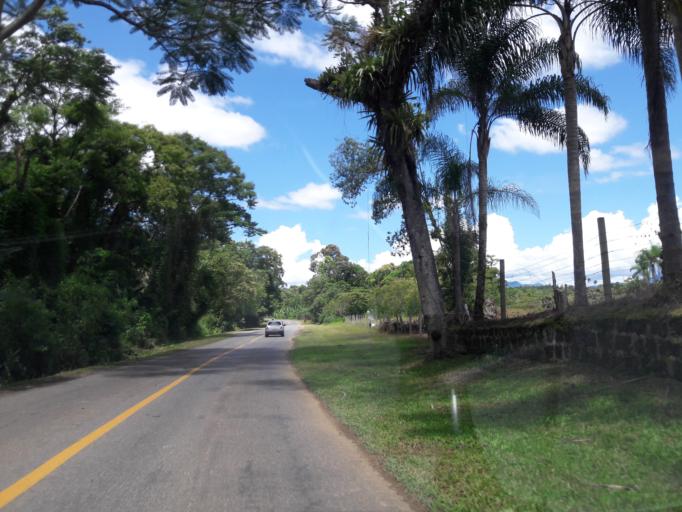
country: BR
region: Parana
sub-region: Antonina
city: Antonina
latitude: -25.4176
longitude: -48.8268
